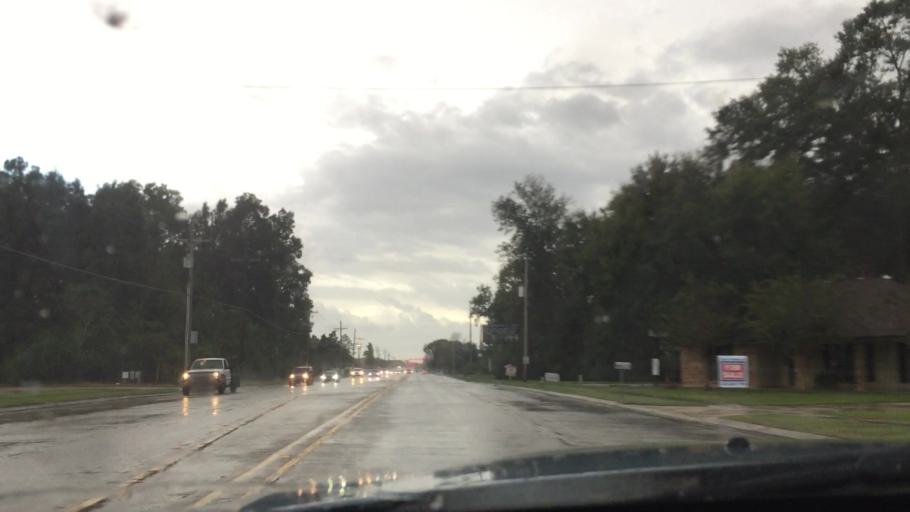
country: US
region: Louisiana
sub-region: East Baton Rouge Parish
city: Monticello
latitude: 30.4507
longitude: -91.0246
